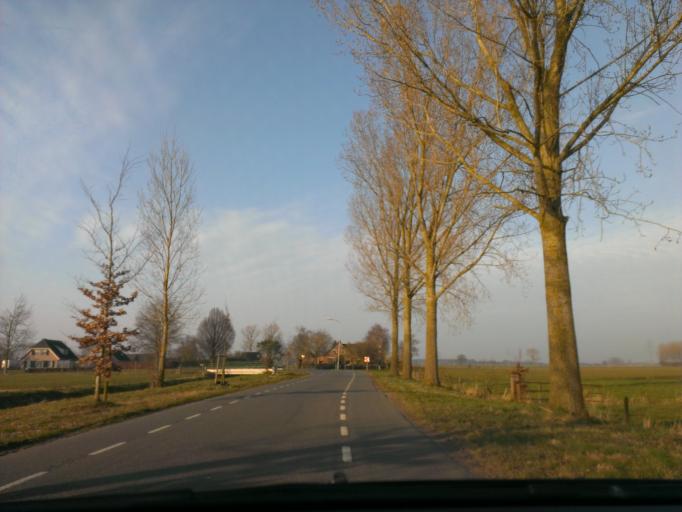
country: NL
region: Gelderland
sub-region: Gemeente Epe
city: Oene
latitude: 52.3388
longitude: 6.0543
